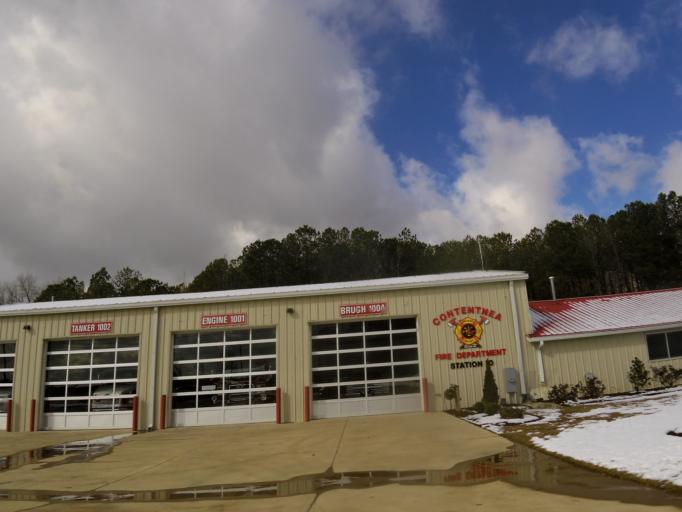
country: US
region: North Carolina
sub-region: Wilson County
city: Wilson
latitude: 35.7207
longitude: -77.9882
